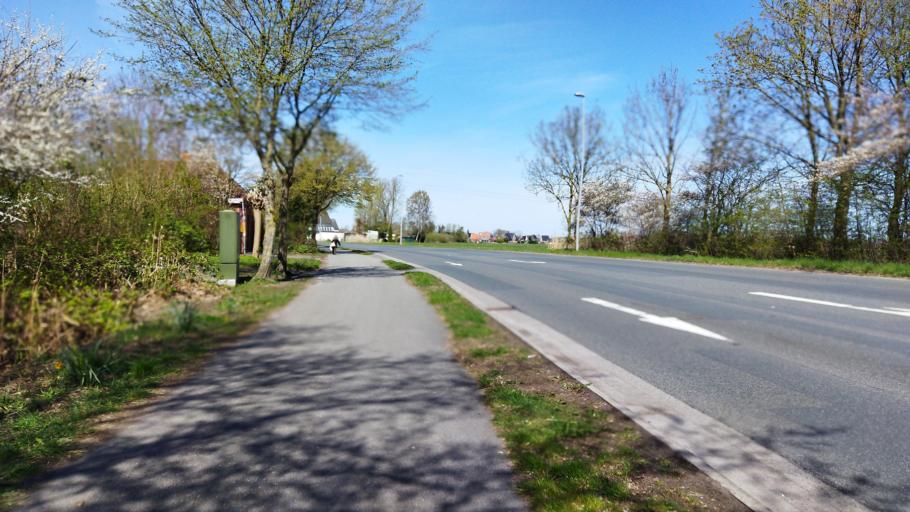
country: DE
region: Lower Saxony
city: Brake (Unterweser)
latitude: 53.3452
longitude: 8.4724
